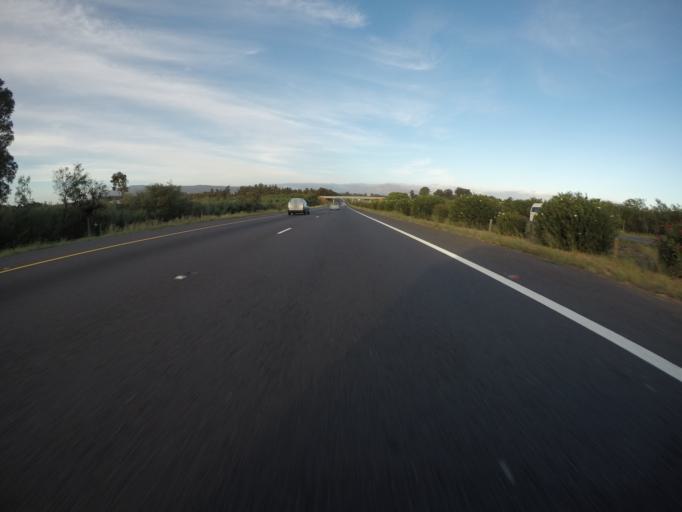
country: ZA
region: Western Cape
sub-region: Cape Winelands District Municipality
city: Stellenbosch
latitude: -33.8023
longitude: 18.8541
